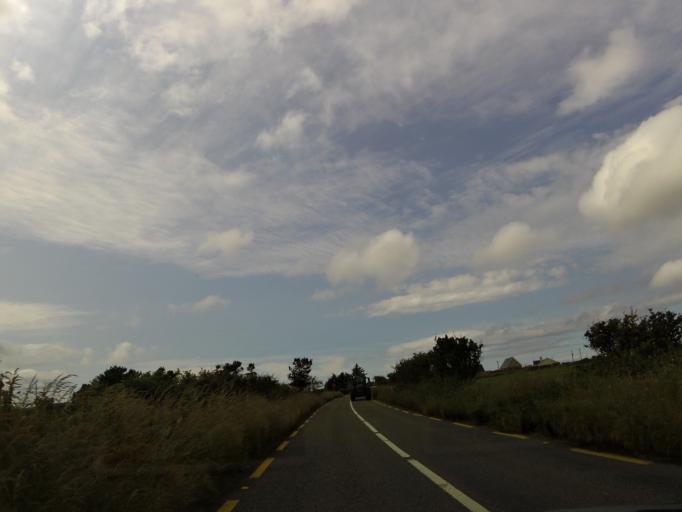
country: IE
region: Munster
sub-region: An Clar
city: Kilrush
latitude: 52.6742
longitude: -9.6083
